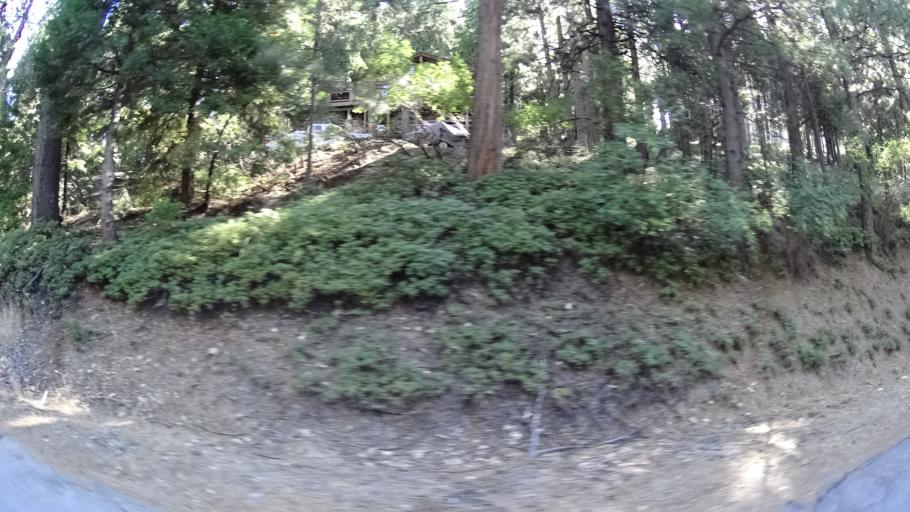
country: US
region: California
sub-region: Calaveras County
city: Arnold
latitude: 38.2554
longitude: -120.3180
